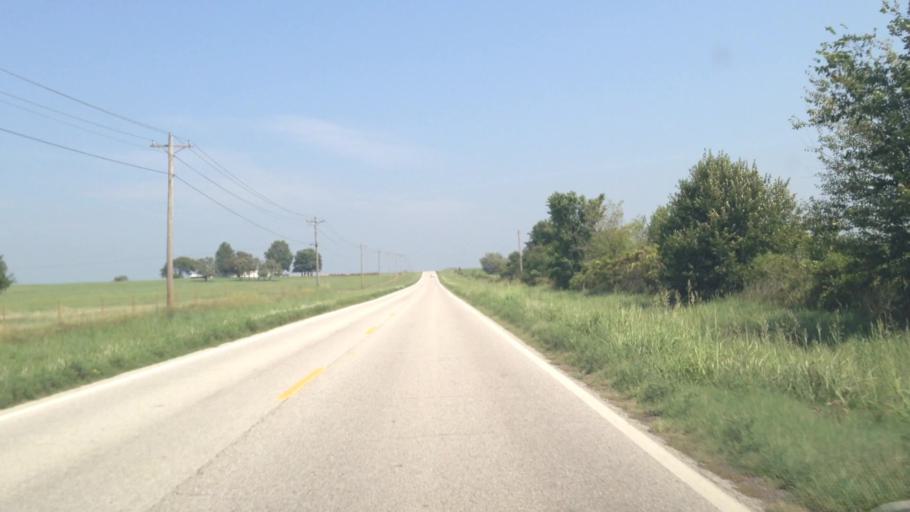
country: US
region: Oklahoma
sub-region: Craig County
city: Vinita
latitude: 36.7346
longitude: -95.1436
